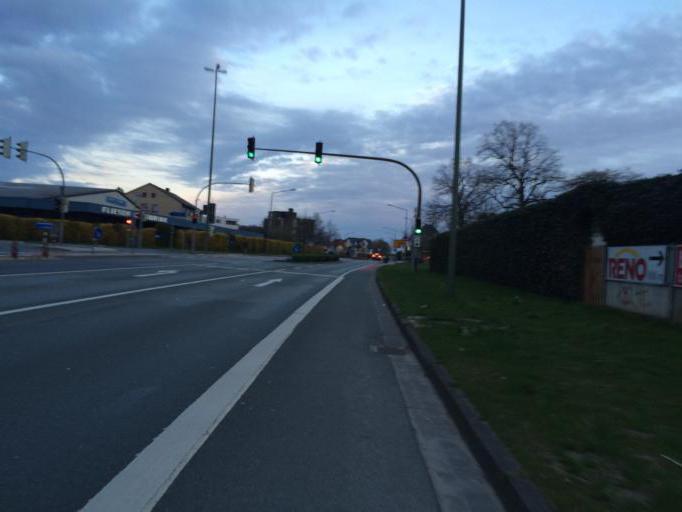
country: DE
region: Lower Saxony
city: Osnabrueck
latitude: 52.2557
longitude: 8.0940
